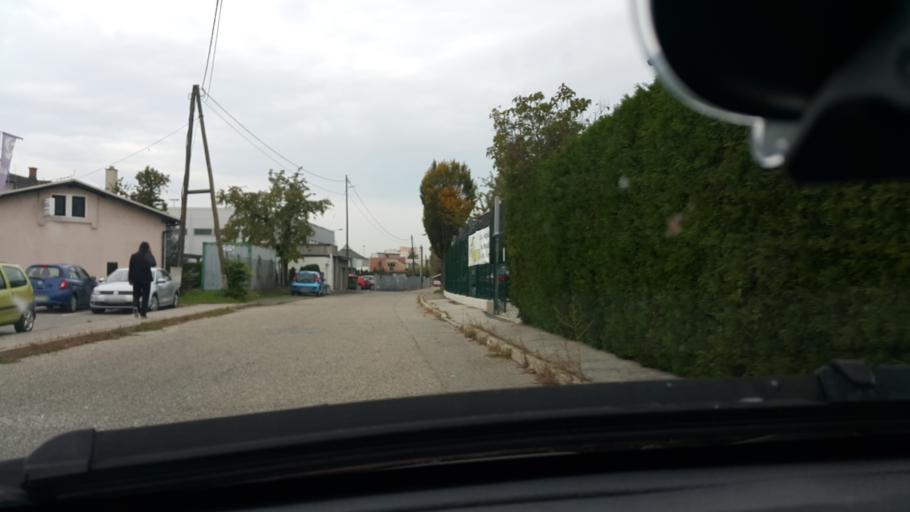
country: SI
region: Hoce-Slivnica
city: Rogoza
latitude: 46.5291
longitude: 15.6730
